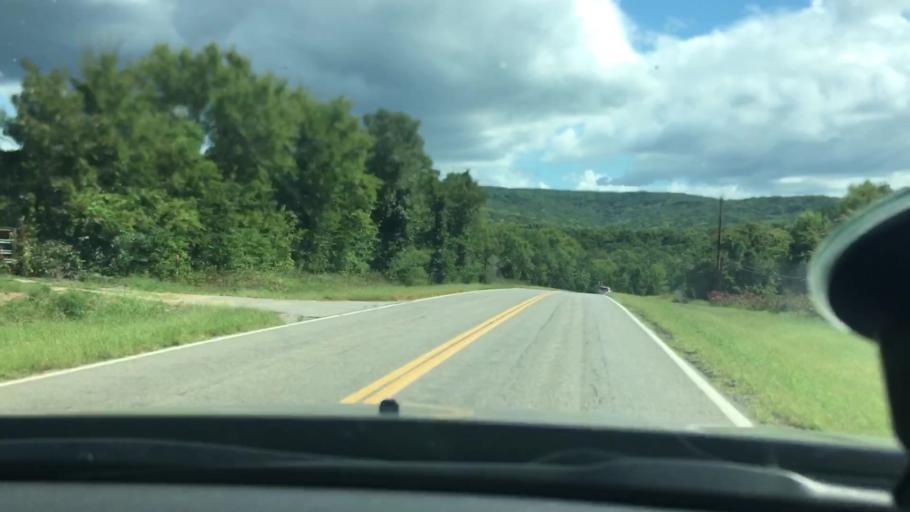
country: US
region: Oklahoma
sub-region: Cherokee County
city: Park Hill
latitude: 35.6901
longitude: -94.9116
